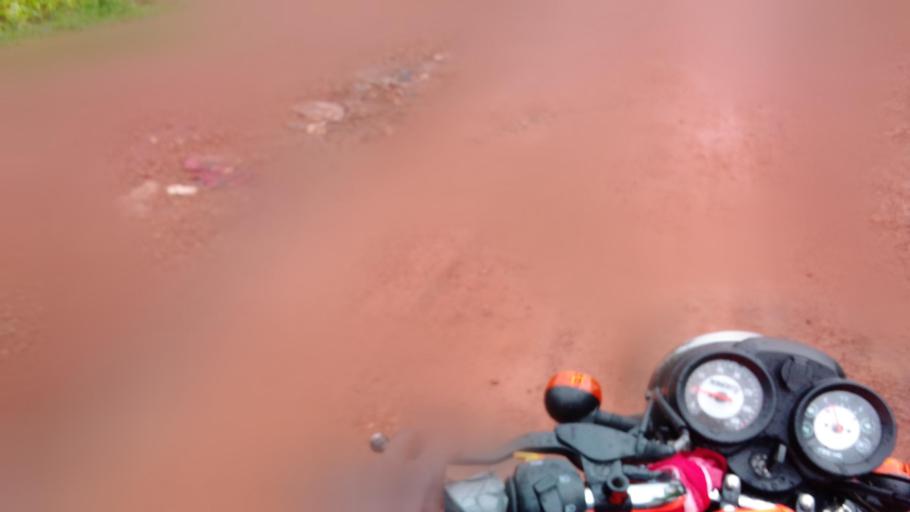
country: SL
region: Eastern Province
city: Kenema
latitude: 7.8643
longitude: -11.1734
